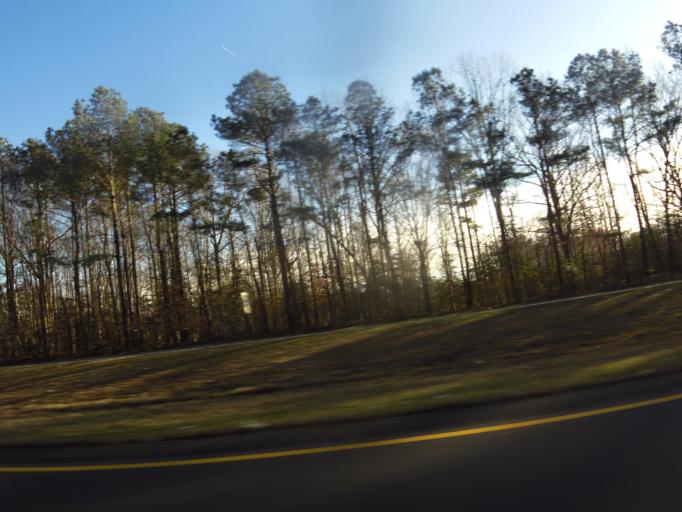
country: US
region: Virginia
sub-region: City of Franklin
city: Franklin
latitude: 36.6503
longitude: -76.8646
